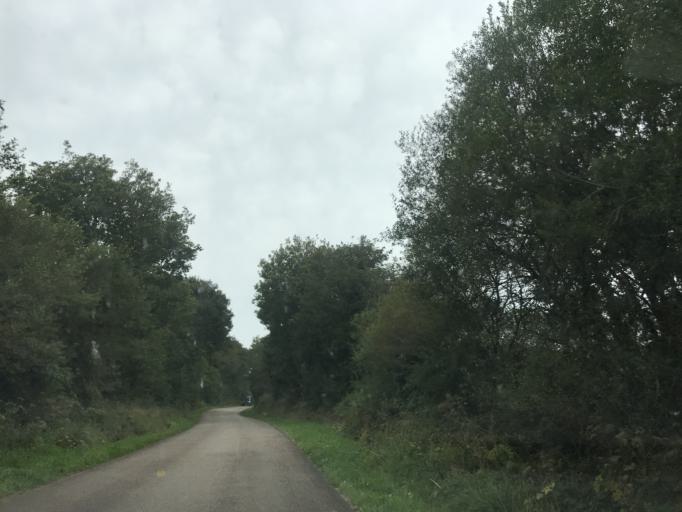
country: FR
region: Brittany
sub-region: Departement du Finistere
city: Plouneour-Menez
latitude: 48.3879
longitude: -3.8958
